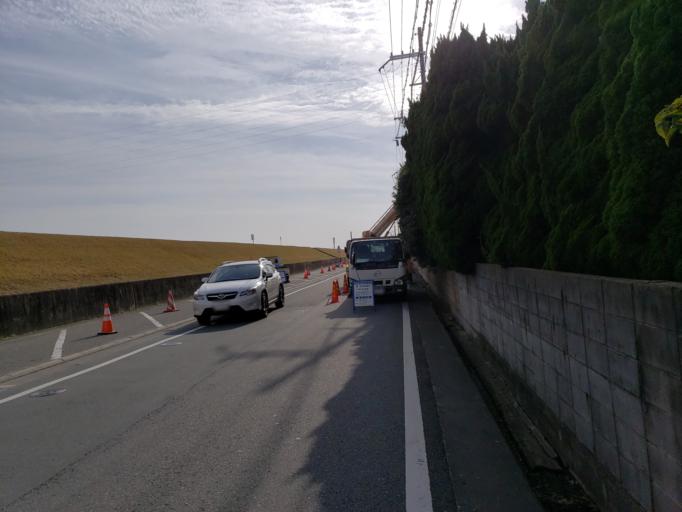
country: JP
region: Hyogo
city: Kakogawacho-honmachi
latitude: 34.7388
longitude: 134.8053
